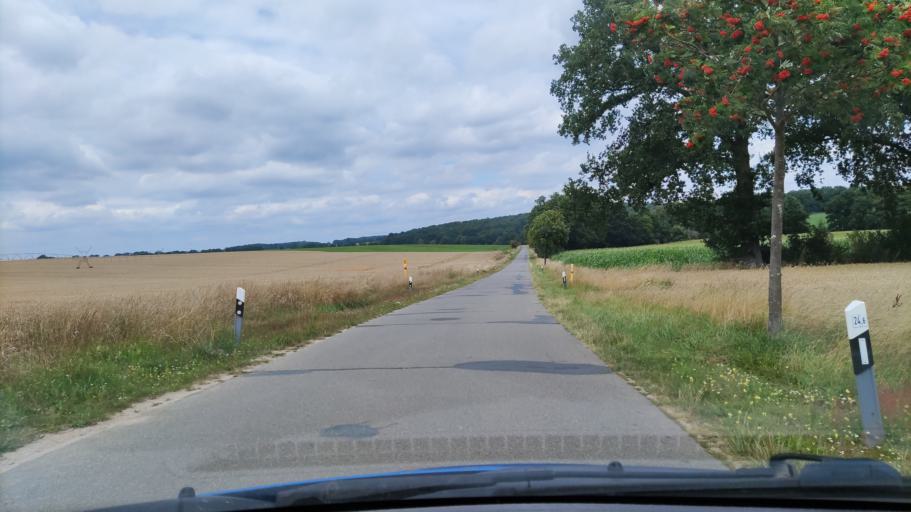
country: DE
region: Lower Saxony
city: Weste
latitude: 53.0723
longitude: 10.6896
